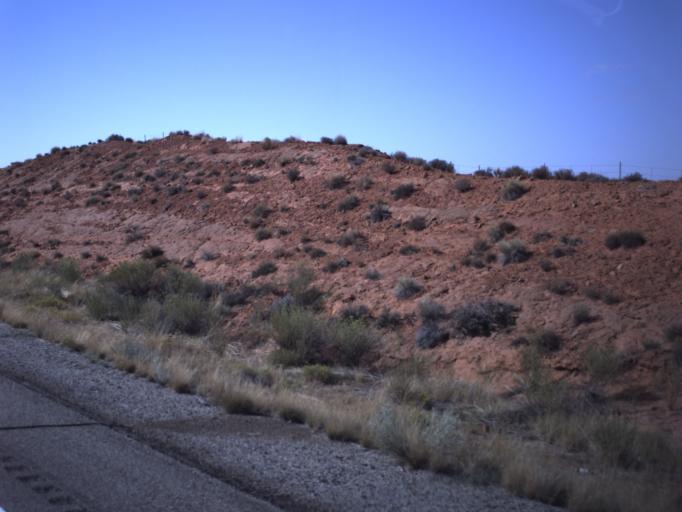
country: US
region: Utah
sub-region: San Juan County
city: Blanding
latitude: 37.2417
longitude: -109.6075
